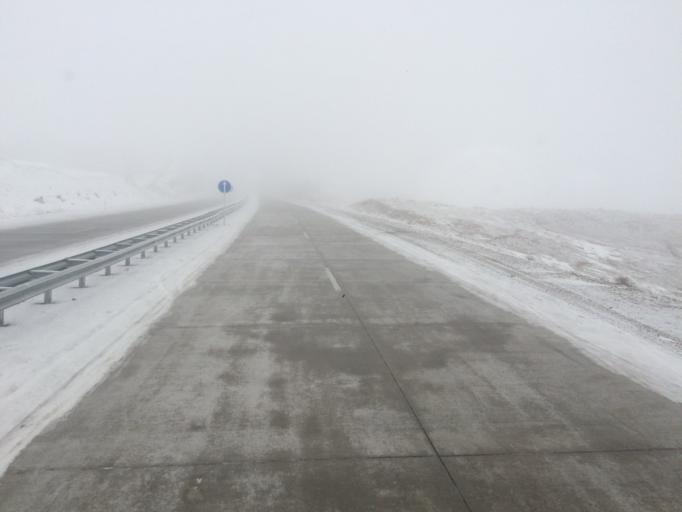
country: KZ
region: Zhambyl
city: Georgiyevka
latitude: 43.4213
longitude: 74.9693
